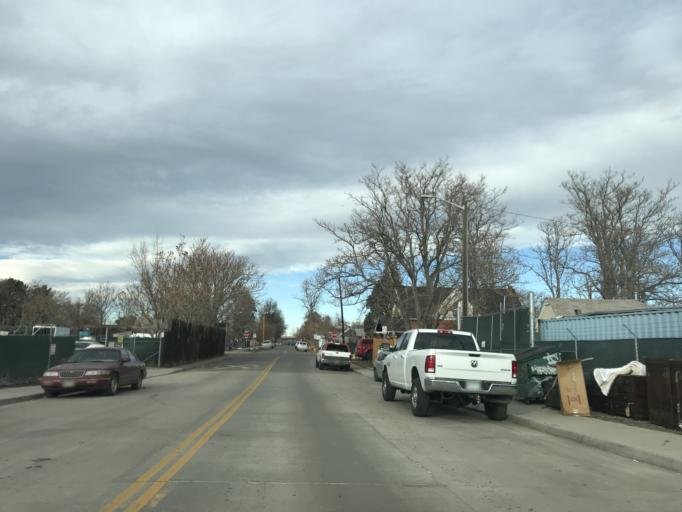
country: US
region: Colorado
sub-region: Adams County
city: Commerce City
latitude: 39.7756
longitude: -104.9542
